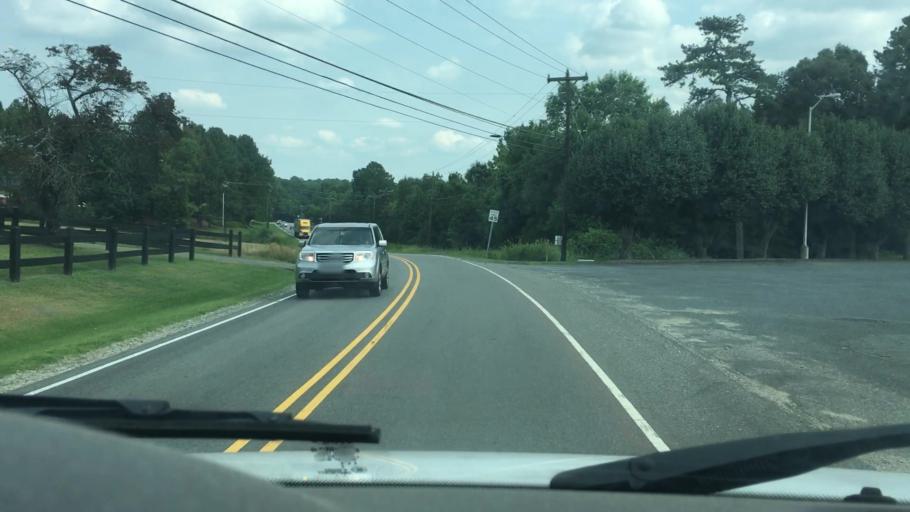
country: US
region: North Carolina
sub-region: Gaston County
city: Davidson
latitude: 35.4662
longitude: -80.8139
